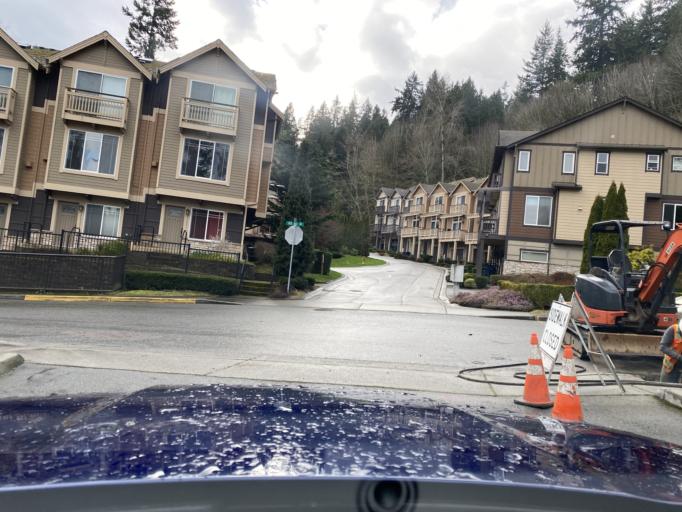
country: US
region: Washington
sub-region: King County
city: Redmond
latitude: 47.6862
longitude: -122.1021
